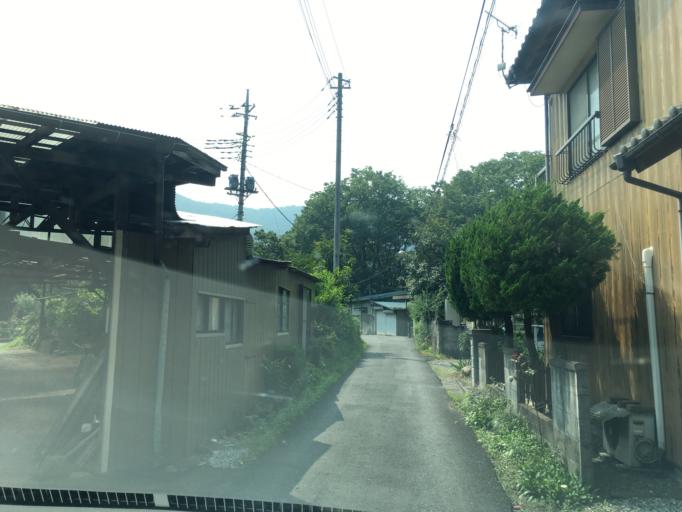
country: JP
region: Saitama
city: Chichibu
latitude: 36.0084
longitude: 139.1095
